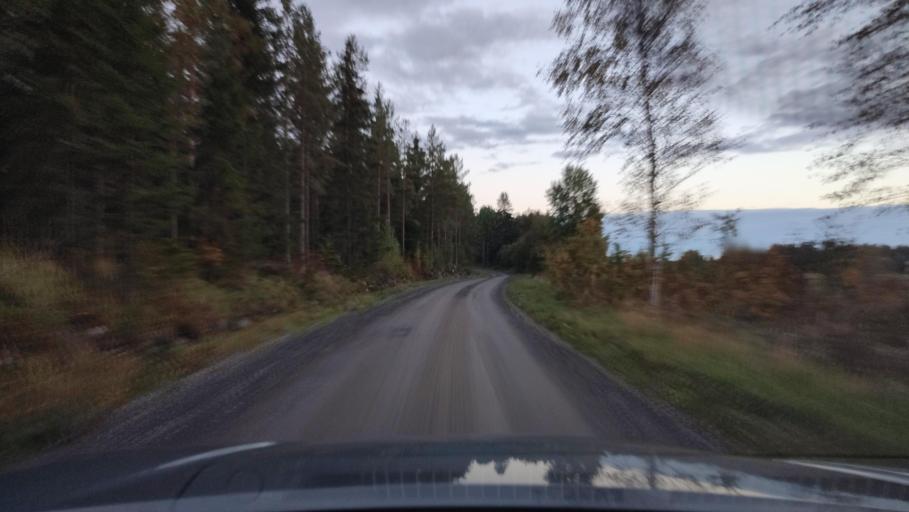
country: FI
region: Ostrobothnia
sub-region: Sydosterbotten
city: Kristinestad
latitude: 62.2792
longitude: 21.5150
